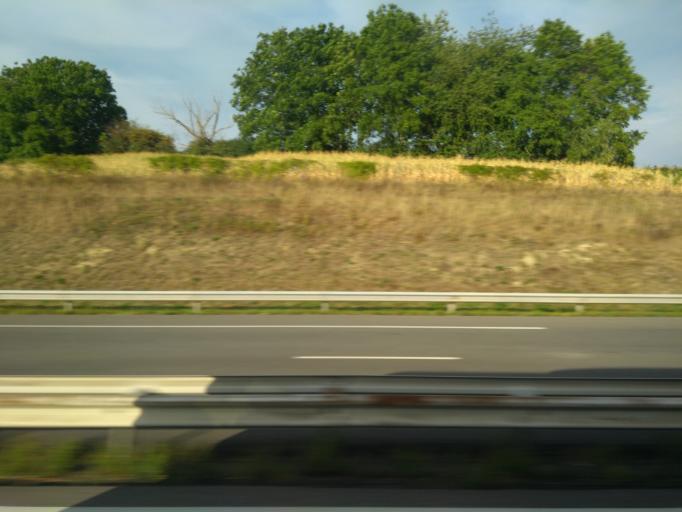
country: FR
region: Rhone-Alpes
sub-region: Departement de l'Isere
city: Cessieu
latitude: 45.5559
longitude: 5.3554
